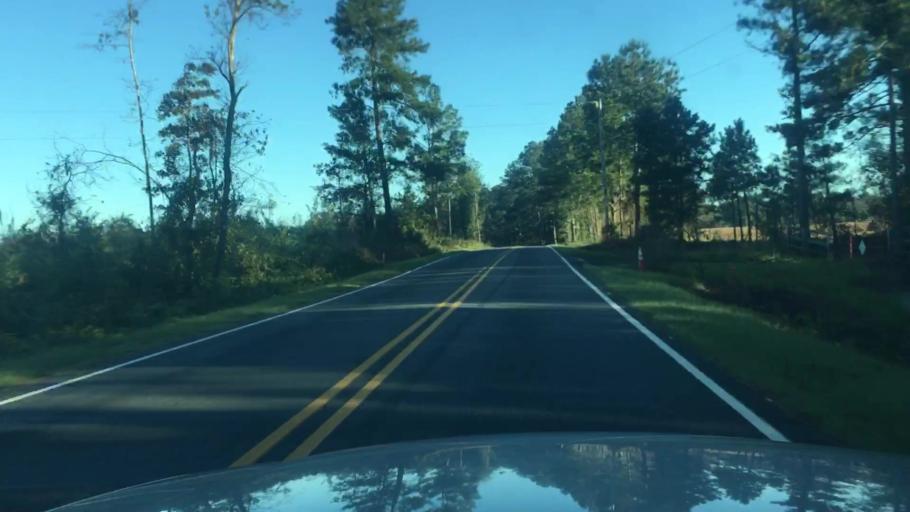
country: US
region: North Carolina
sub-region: Harnett County
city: Walkertown
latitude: 35.2861
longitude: -78.8694
